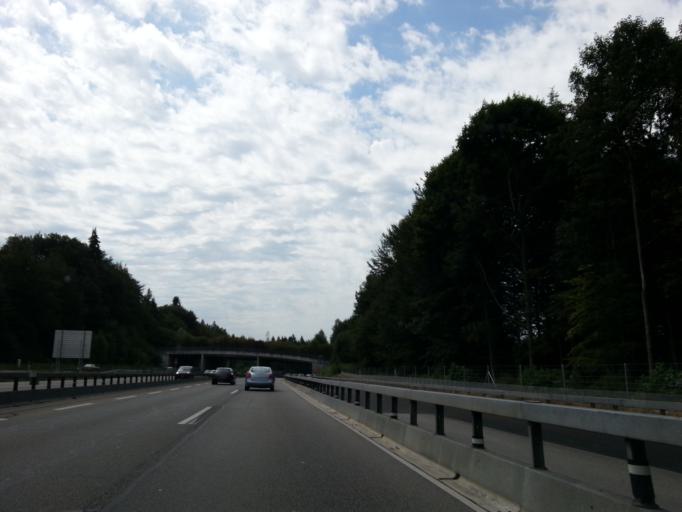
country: CH
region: Bern
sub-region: Emmental District
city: Lyssach
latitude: 47.0639
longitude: 7.5599
